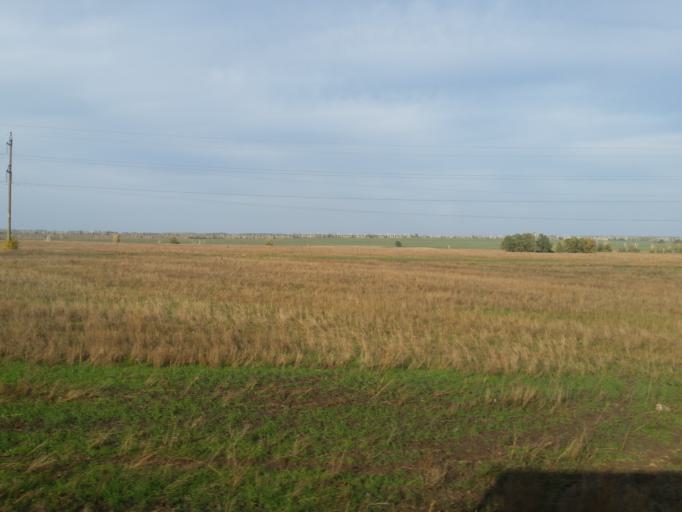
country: RU
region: Ulyanovsk
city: Mullovka
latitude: 54.2678
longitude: 49.1652
